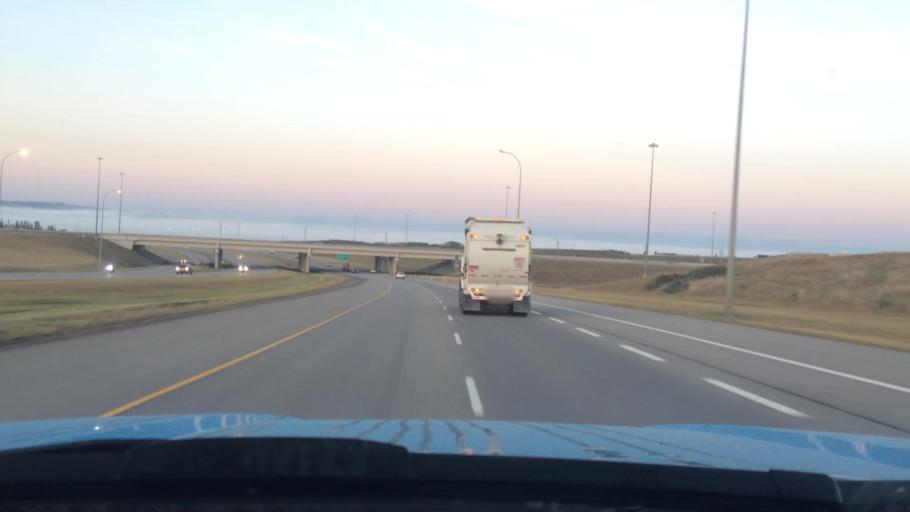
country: CA
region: Alberta
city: Calgary
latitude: 51.1343
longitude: -114.2243
